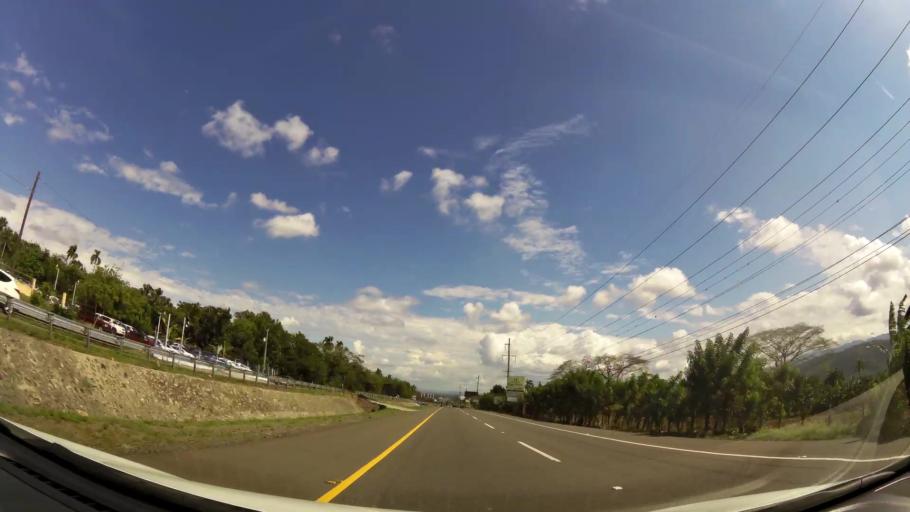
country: DO
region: La Vega
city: Concepcion de La Vega
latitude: 19.2548
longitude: -70.5637
